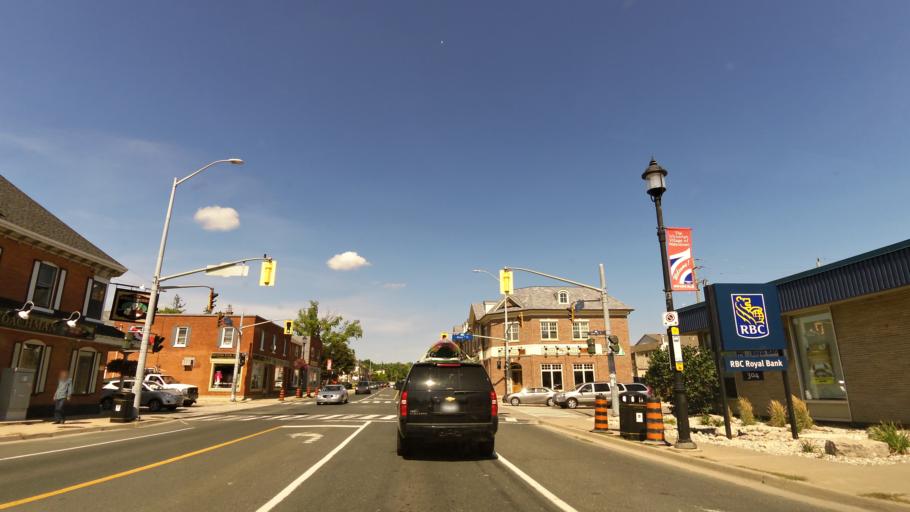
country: CA
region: Ontario
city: Burlington
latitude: 43.3331
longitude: -79.8931
